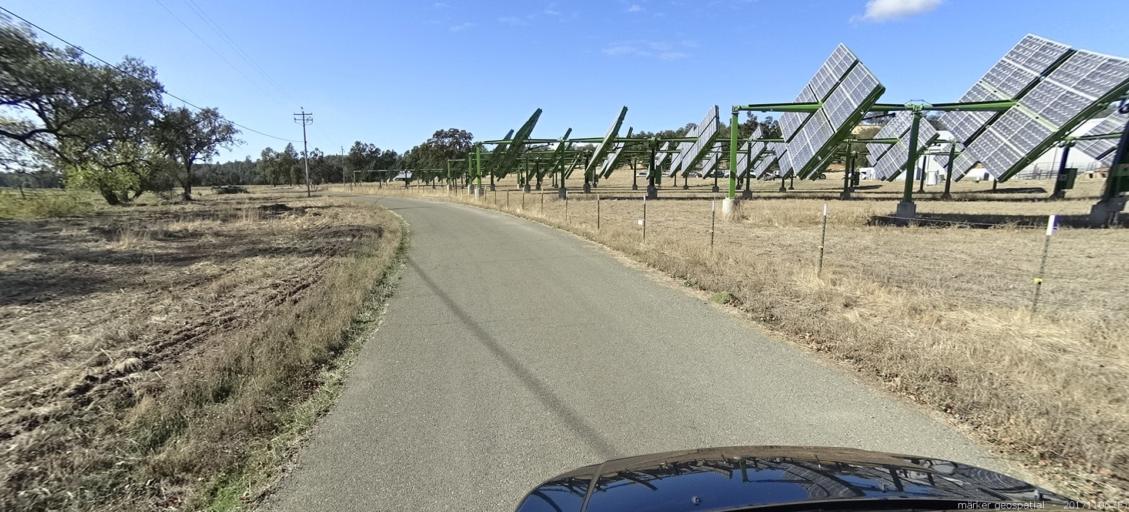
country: US
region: California
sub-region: Shasta County
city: Bella Vista
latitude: 40.6296
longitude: -122.2234
